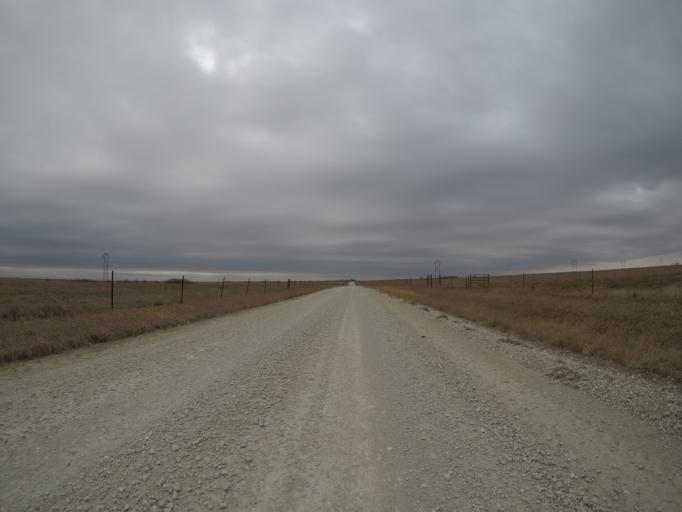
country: US
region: Kansas
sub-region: Wabaunsee County
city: Alma
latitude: 38.7561
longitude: -96.1496
